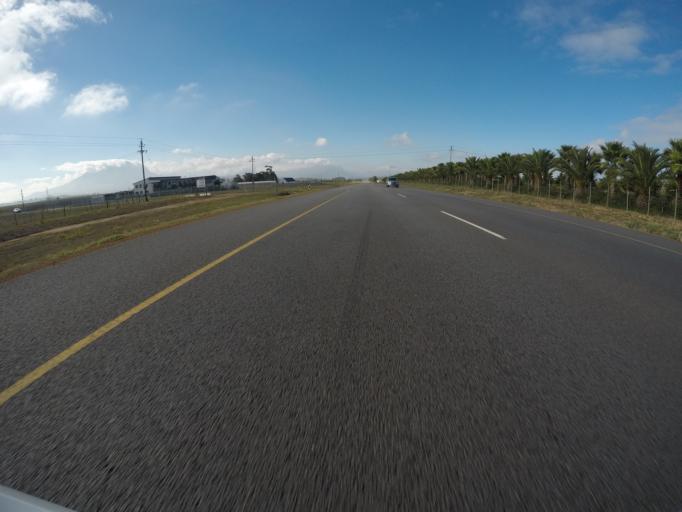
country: ZA
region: Western Cape
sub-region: City of Cape Town
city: Kraaifontein
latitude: -33.8390
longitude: 18.7992
